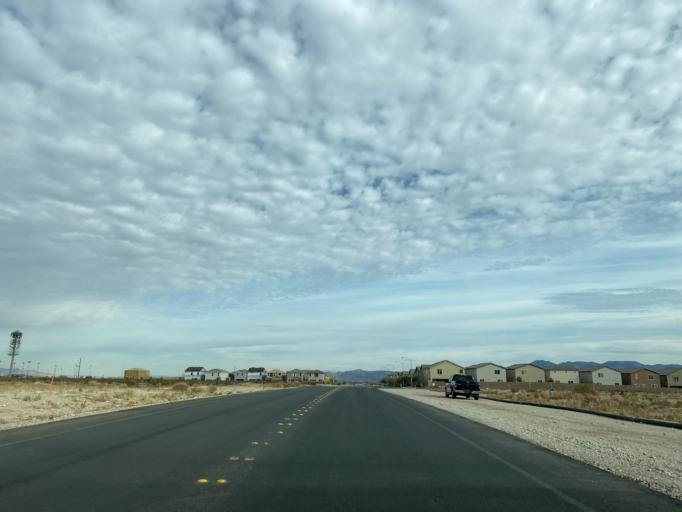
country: US
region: Nevada
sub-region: Clark County
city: Enterprise
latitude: 35.9982
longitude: -115.2784
